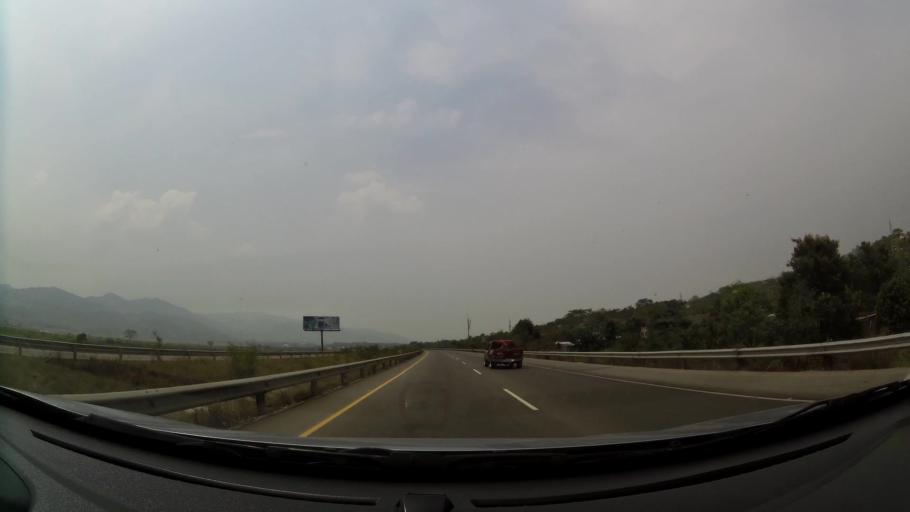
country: HN
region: Cortes
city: El Plan
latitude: 15.2875
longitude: -87.9775
